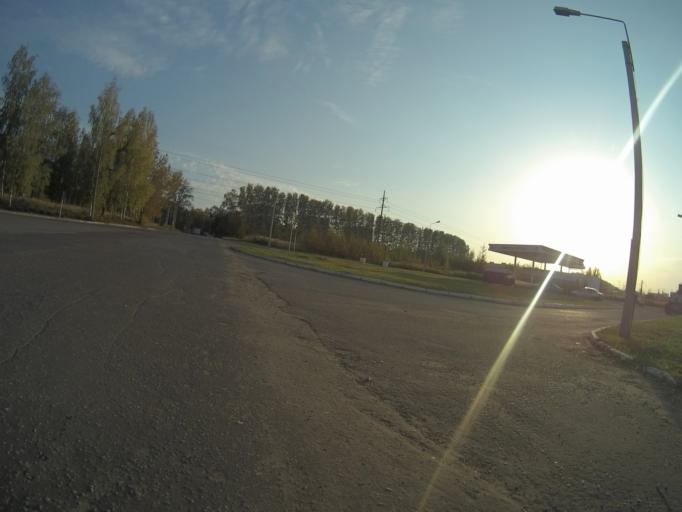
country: RU
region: Vladimir
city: Bogolyubovo
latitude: 56.1763
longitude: 40.4802
